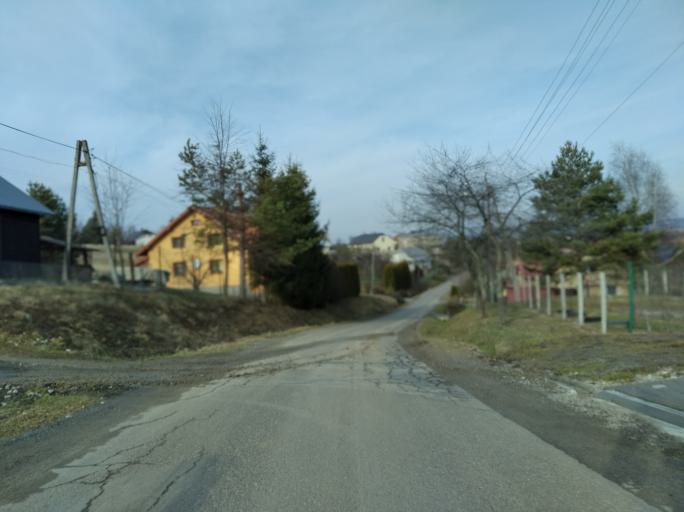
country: PL
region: Subcarpathian Voivodeship
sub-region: Powiat brzozowski
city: Turze Pole
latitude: 49.6796
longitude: 22.0039
